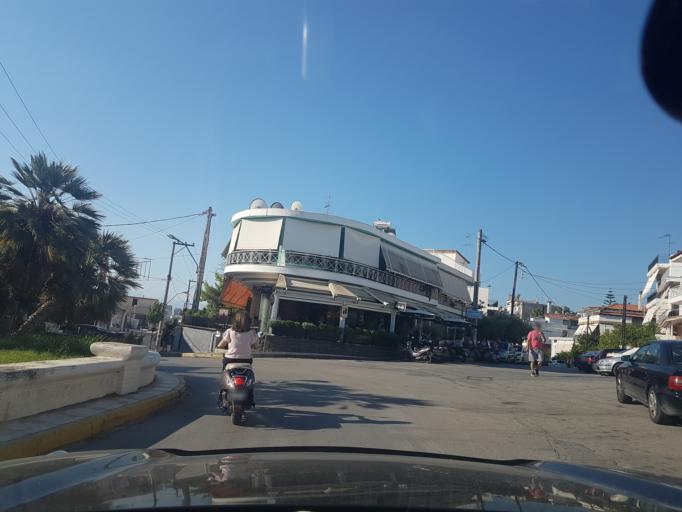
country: GR
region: Central Greece
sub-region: Nomos Evvoias
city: Chalkida
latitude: 38.4707
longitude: 23.5864
